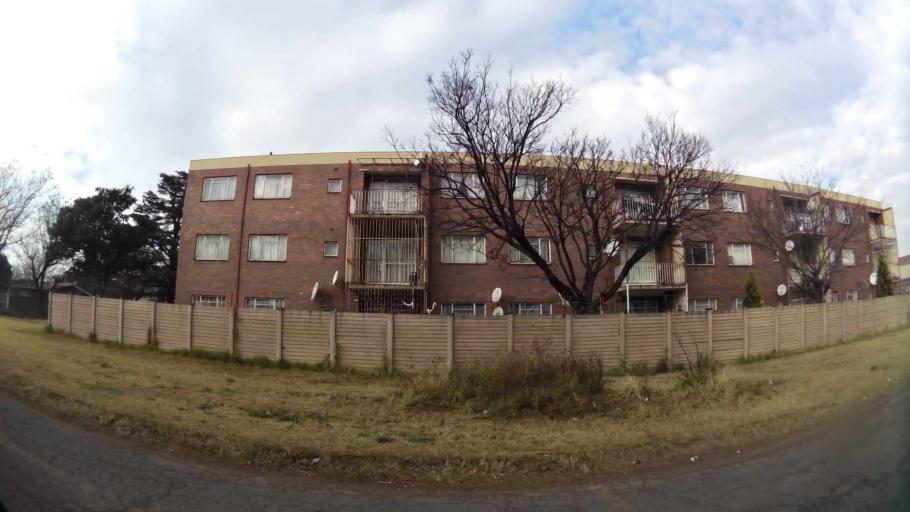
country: ZA
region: Gauteng
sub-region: Sedibeng District Municipality
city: Vanderbijlpark
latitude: -26.6817
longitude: 27.8121
